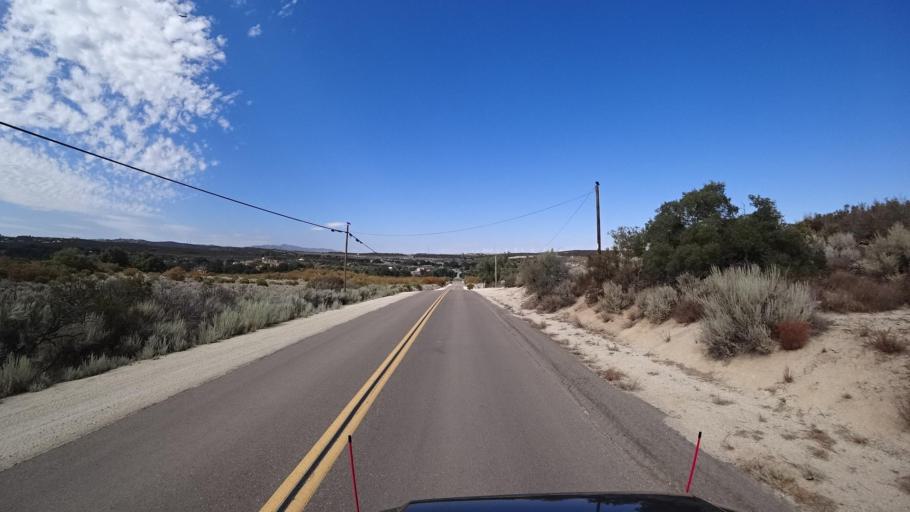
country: MX
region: Baja California
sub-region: Tecate
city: Cereso del Hongo
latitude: 32.6641
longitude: -116.2902
